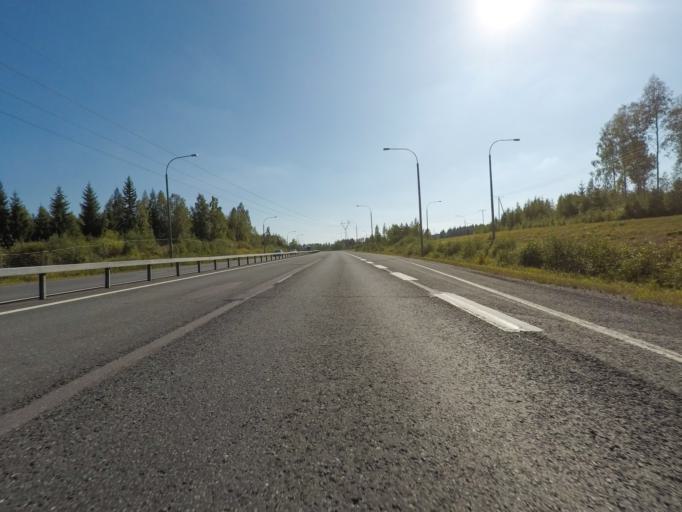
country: FI
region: Northern Savo
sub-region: Kuopio
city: Kuopio
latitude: 62.7002
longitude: 27.5669
